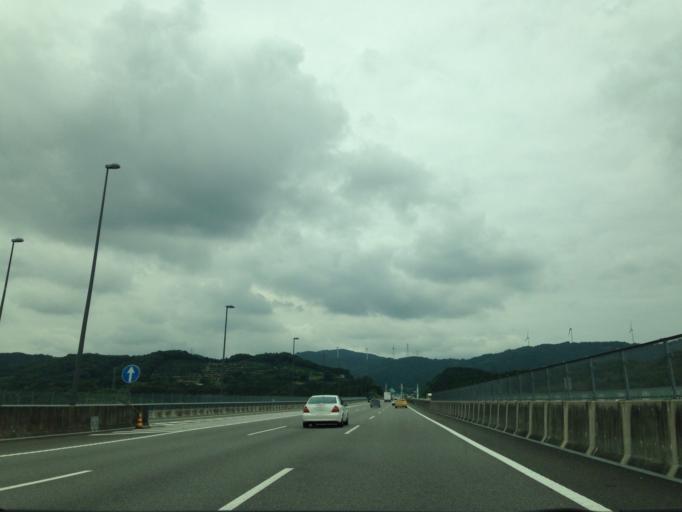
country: JP
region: Shizuoka
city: Hamakita
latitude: 34.8446
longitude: 137.7401
